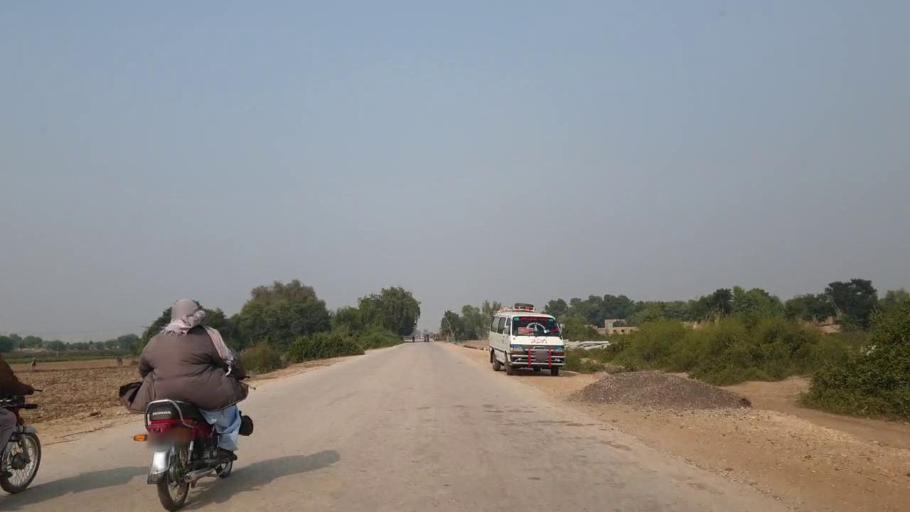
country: PK
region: Sindh
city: Bhan
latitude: 26.5754
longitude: 67.7277
